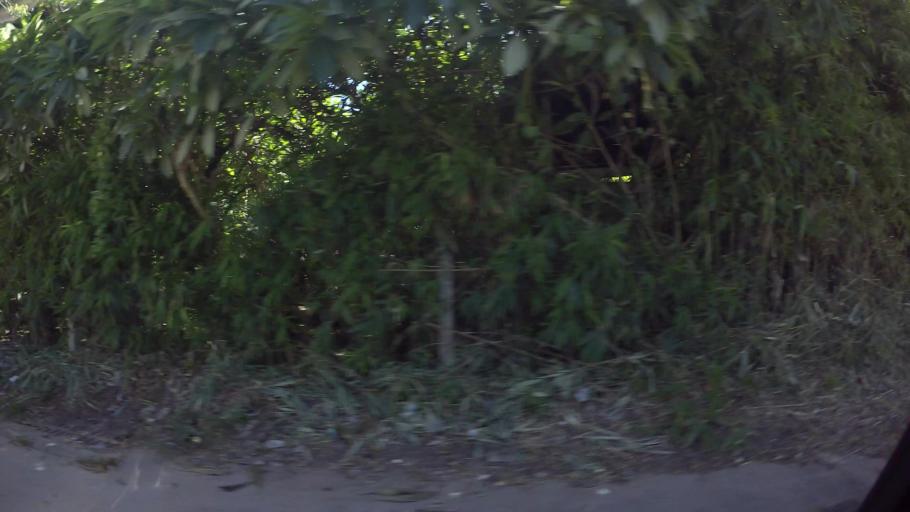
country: TH
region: Chon Buri
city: Phatthaya
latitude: 12.9322
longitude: 100.8960
